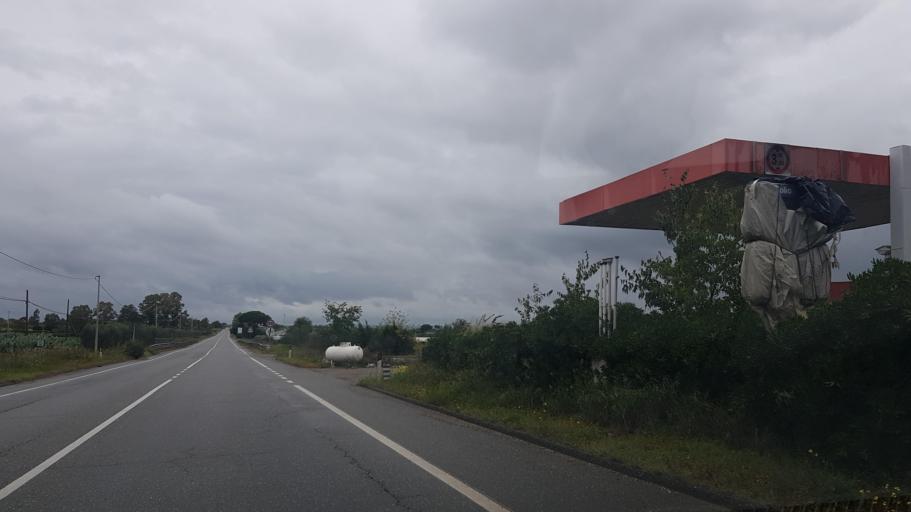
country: IT
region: Apulia
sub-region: Provincia di Taranto
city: Marina di Ginosa
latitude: 40.4051
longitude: 16.8052
